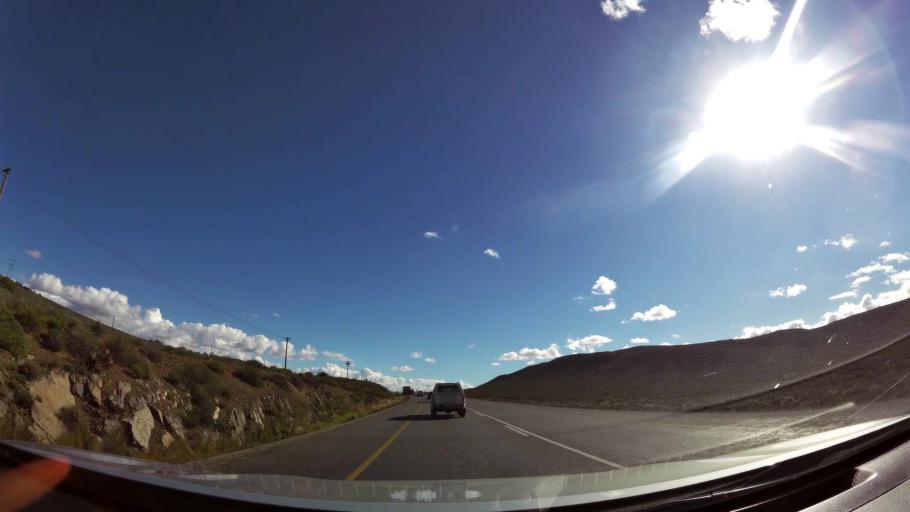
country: ZA
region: Western Cape
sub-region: Cape Winelands District Municipality
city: Worcester
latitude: -33.7348
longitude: 19.6699
